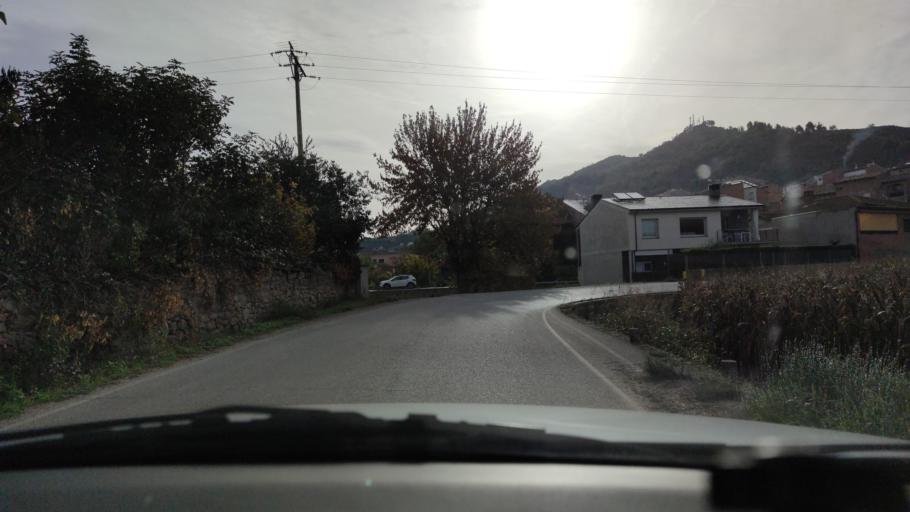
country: ES
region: Catalonia
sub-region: Provincia de Lleida
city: Artesa de Segre
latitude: 41.8981
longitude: 1.0484
